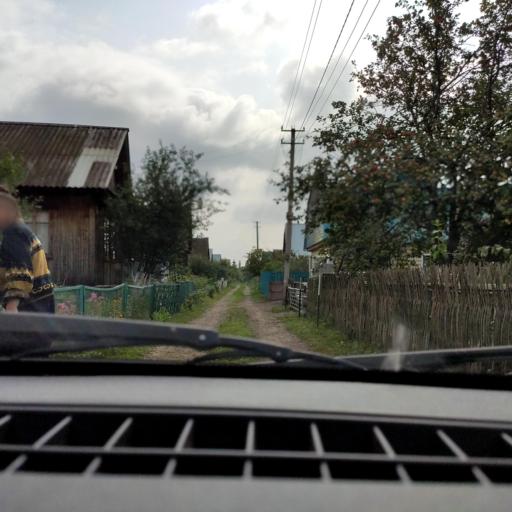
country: RU
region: Bashkortostan
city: Mikhaylovka
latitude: 54.8321
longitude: 55.8326
